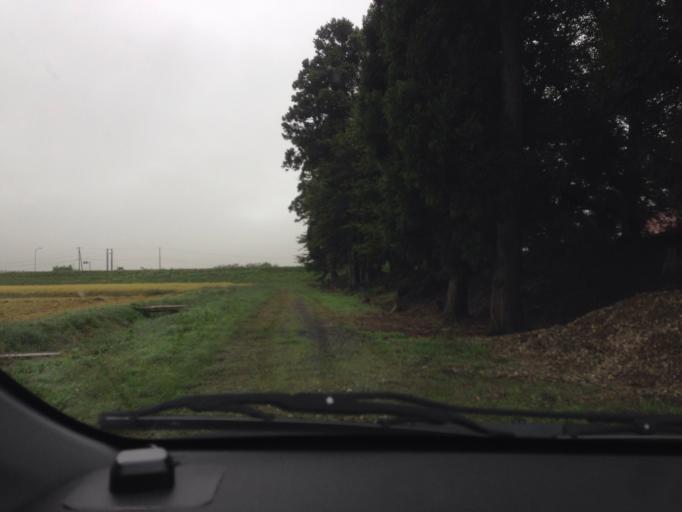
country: JP
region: Fukushima
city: Kitakata
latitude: 37.5890
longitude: 139.8684
